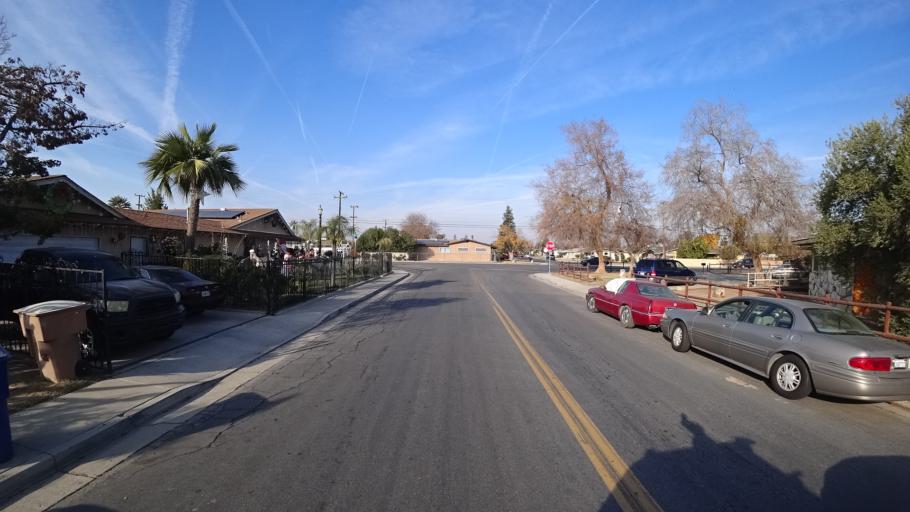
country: US
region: California
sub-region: Kern County
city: Bakersfield
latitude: 35.3245
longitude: -119.0315
